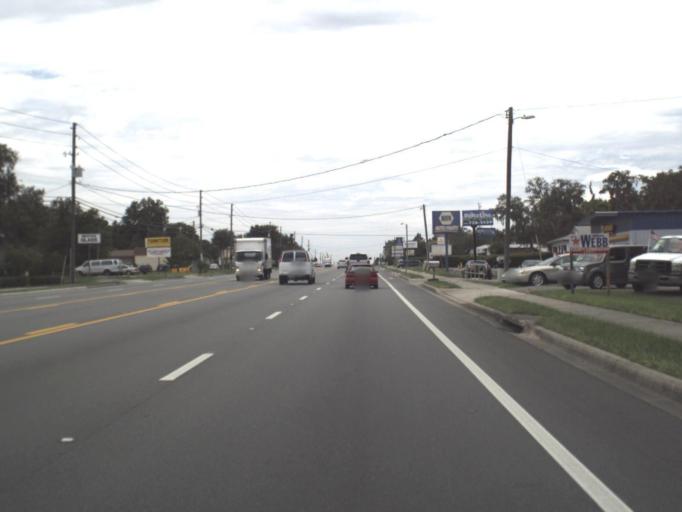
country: US
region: Florida
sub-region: Citrus County
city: Inverness Highlands North
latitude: 28.8403
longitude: -82.3598
